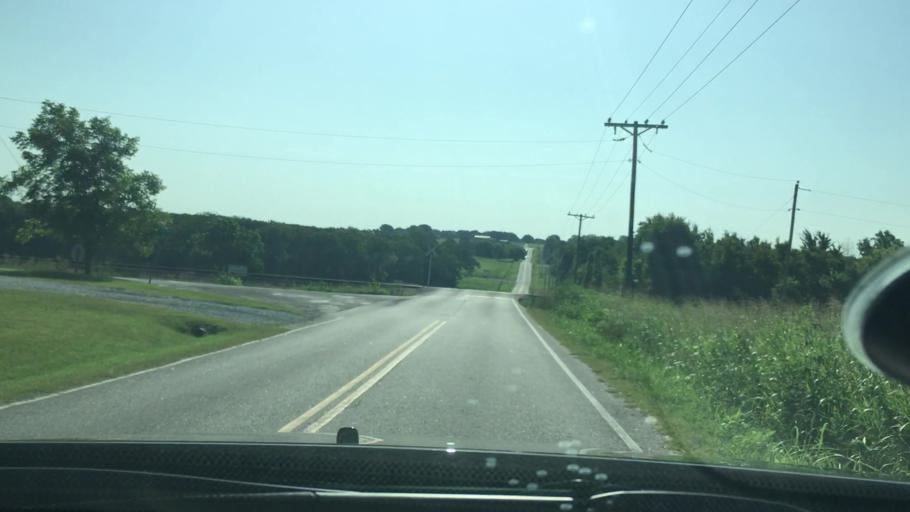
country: US
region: Oklahoma
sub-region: Pontotoc County
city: Ada
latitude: 34.8105
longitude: -96.6268
